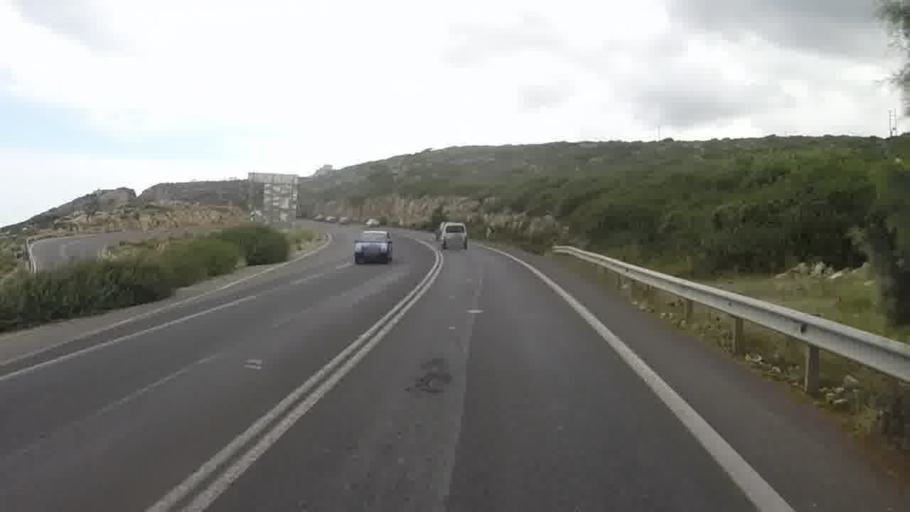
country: GR
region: Crete
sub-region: Nomos Rethymnis
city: Atsipopoulon
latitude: 35.3582
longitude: 24.4079
